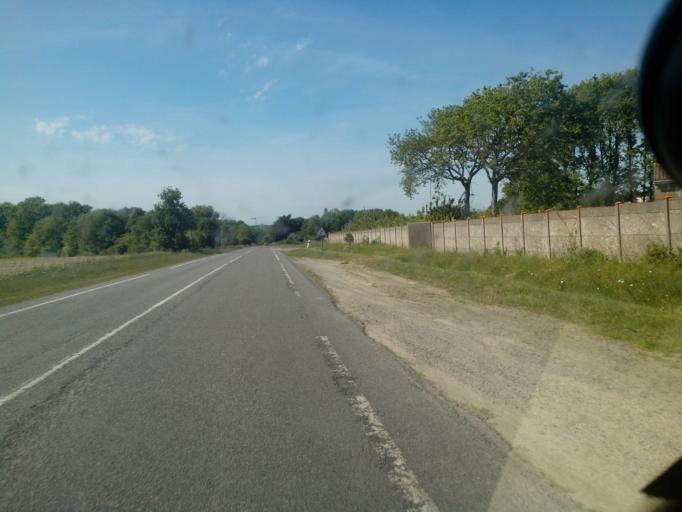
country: FR
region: Pays de la Loire
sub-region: Departement de la Loire-Atlantique
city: Pornic
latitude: 47.1072
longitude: -2.0736
